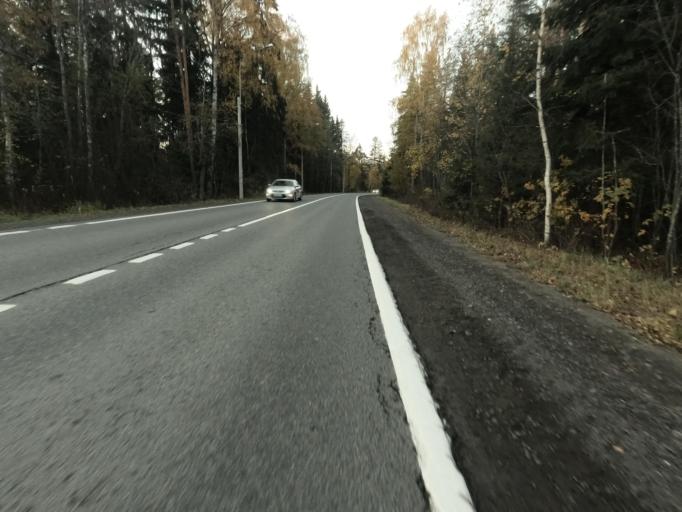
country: RU
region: St.-Petersburg
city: Repino
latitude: 60.1926
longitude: 29.8562
